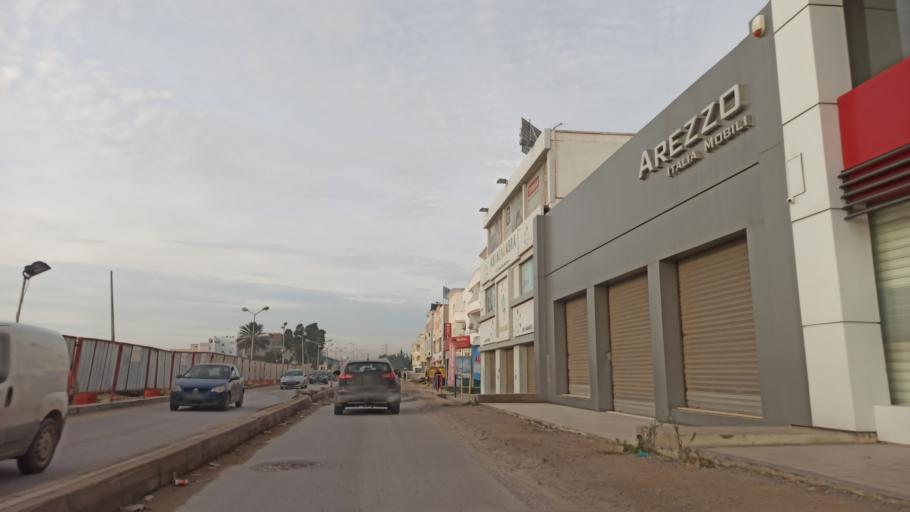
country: TN
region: Ariana
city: Ariana
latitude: 36.8699
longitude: 10.2293
